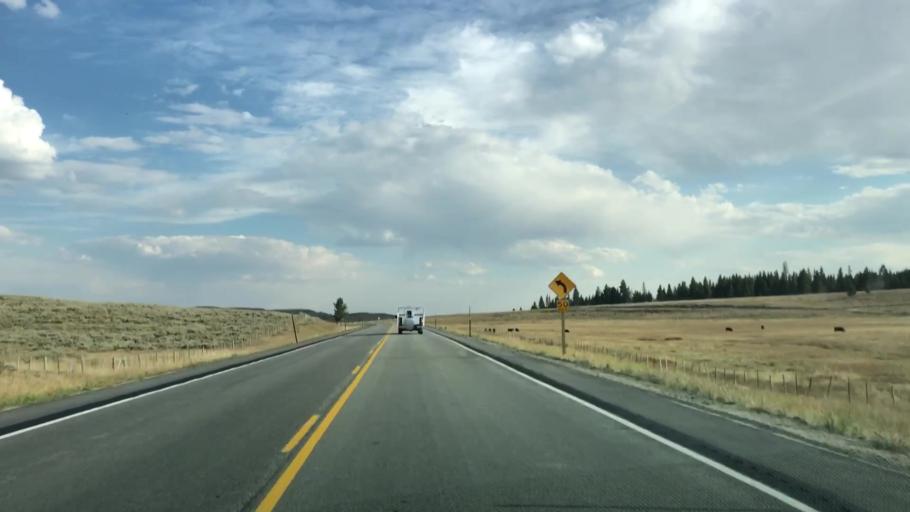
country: US
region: Wyoming
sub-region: Sublette County
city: Pinedale
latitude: 43.1288
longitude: -110.1908
